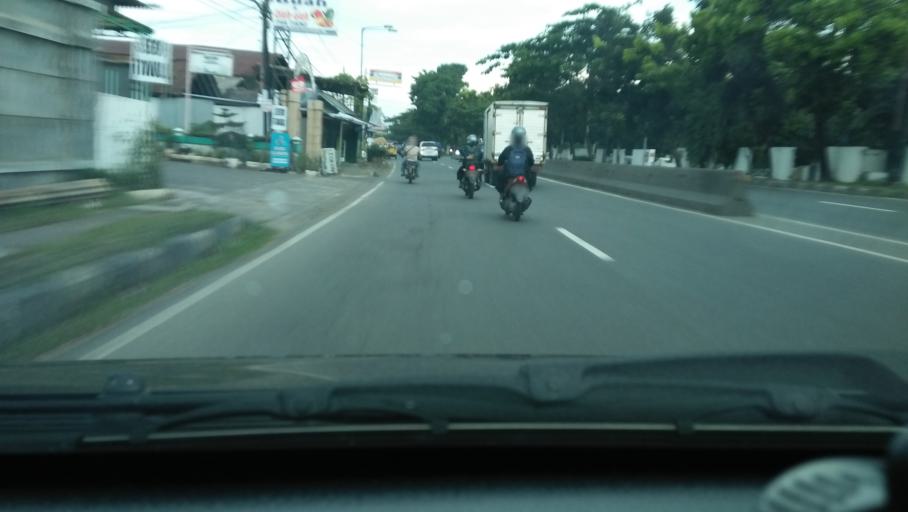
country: ID
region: Central Java
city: Ungaran
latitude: -7.1063
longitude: 110.4109
